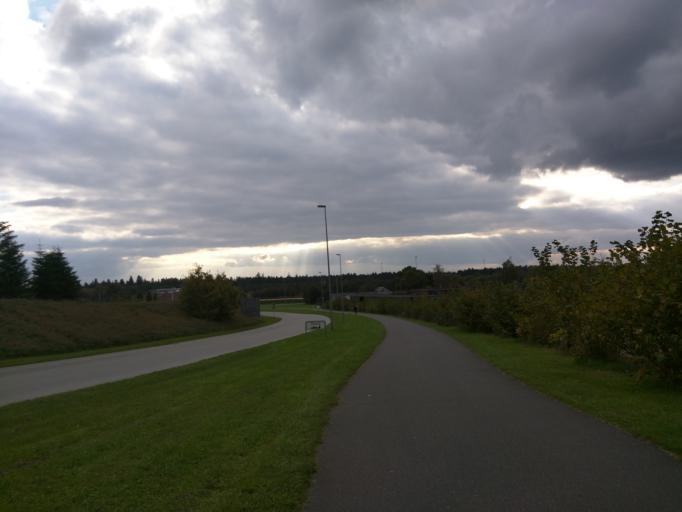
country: DK
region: Central Jutland
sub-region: Viborg Kommune
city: Viborg
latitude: 56.4359
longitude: 9.3799
